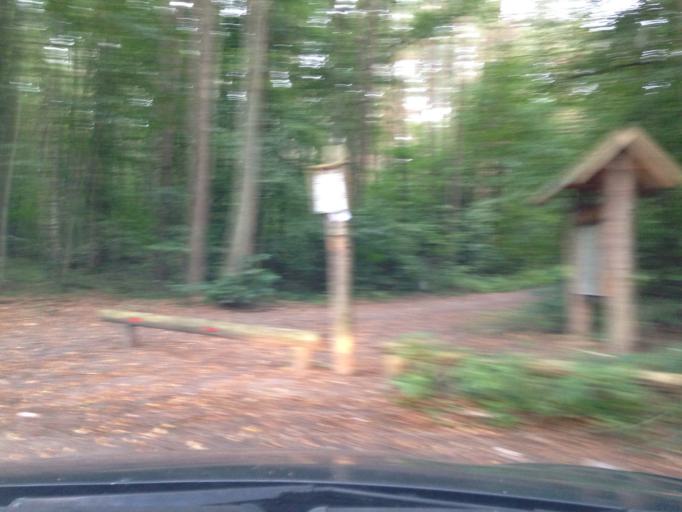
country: DE
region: Mecklenburg-Vorpommern
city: Carpin
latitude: 53.3539
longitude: 13.2297
